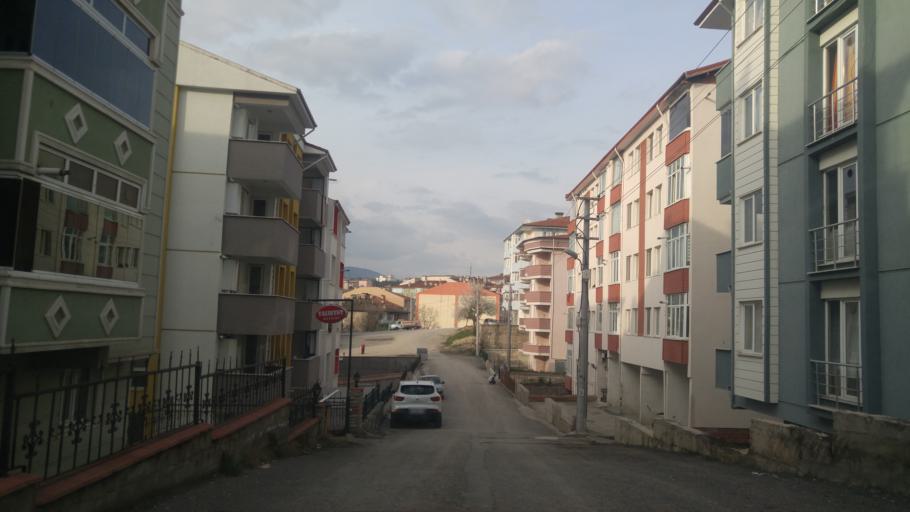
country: TR
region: Karabuk
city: Safranbolu
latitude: 41.2240
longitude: 32.6653
